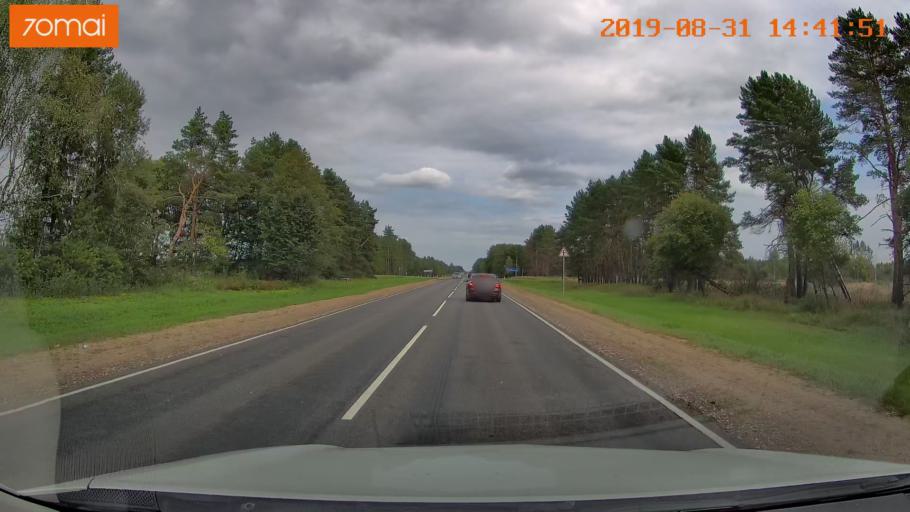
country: RU
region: Smolensk
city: Yekimovichi
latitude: 54.2050
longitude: 33.5980
